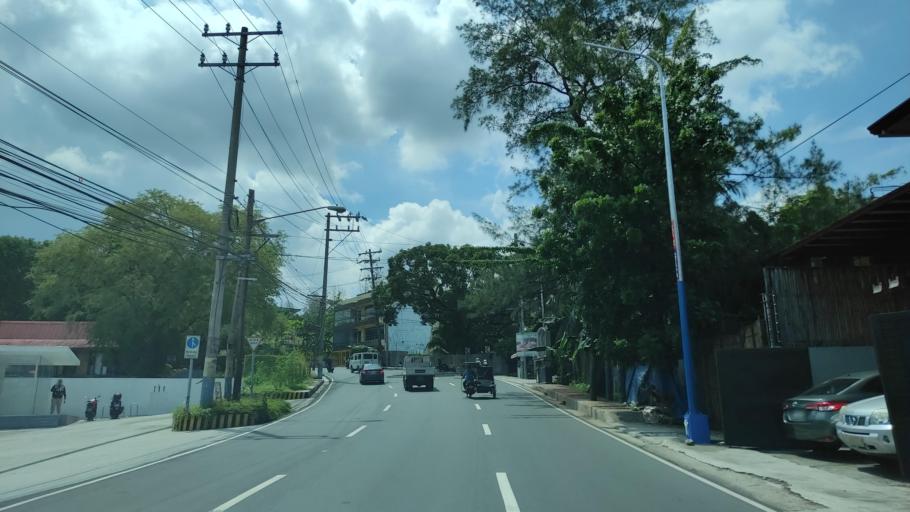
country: PH
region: Calabarzon
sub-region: Province of Rizal
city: Taytay
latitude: 14.5863
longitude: 121.1636
